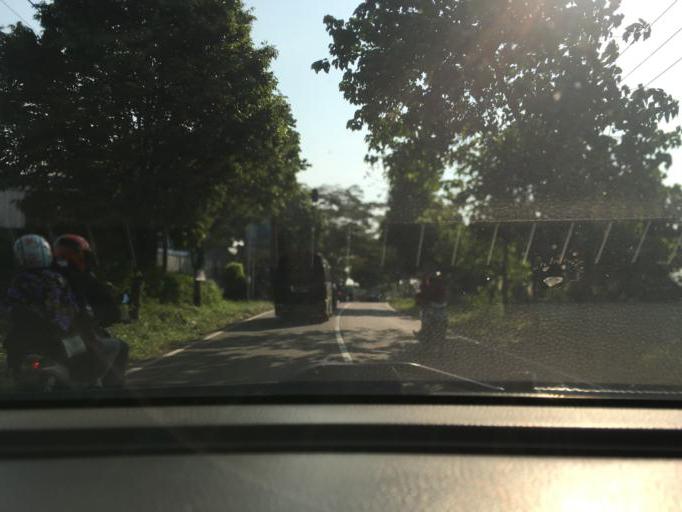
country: ID
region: West Java
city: Kuningan
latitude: -6.8988
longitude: 108.4913
